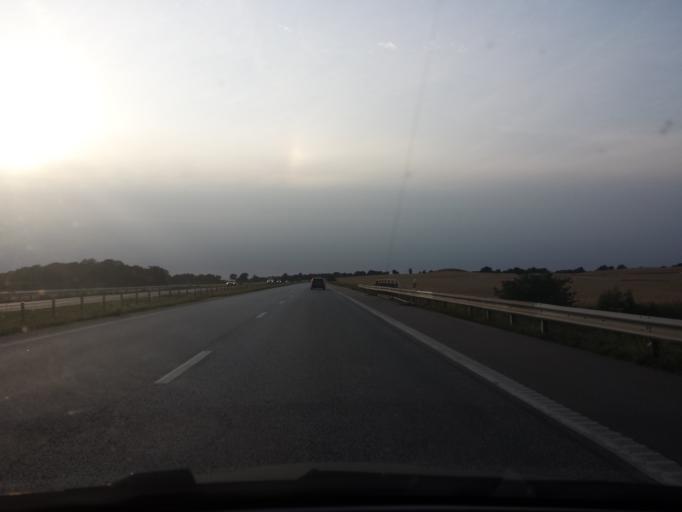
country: SE
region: Skane
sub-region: Svedala Kommun
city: Svedala
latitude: 55.5369
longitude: 13.1721
